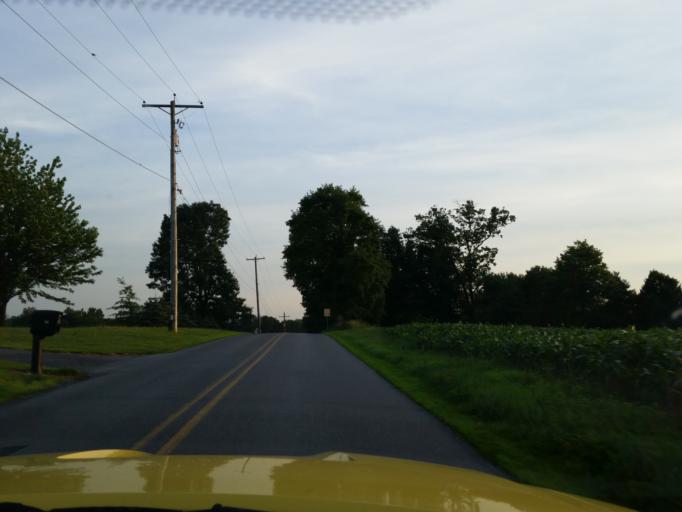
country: US
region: Pennsylvania
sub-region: Lebanon County
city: Fredericksburg
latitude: 40.4217
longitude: -76.4491
